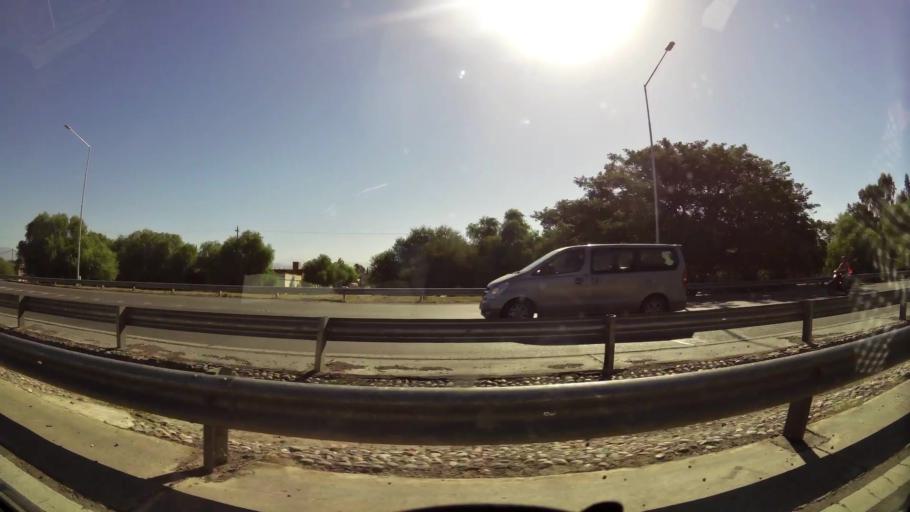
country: AR
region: San Juan
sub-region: Departamento de Santa Lucia
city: Santa Lucia
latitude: -31.5300
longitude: -68.5039
